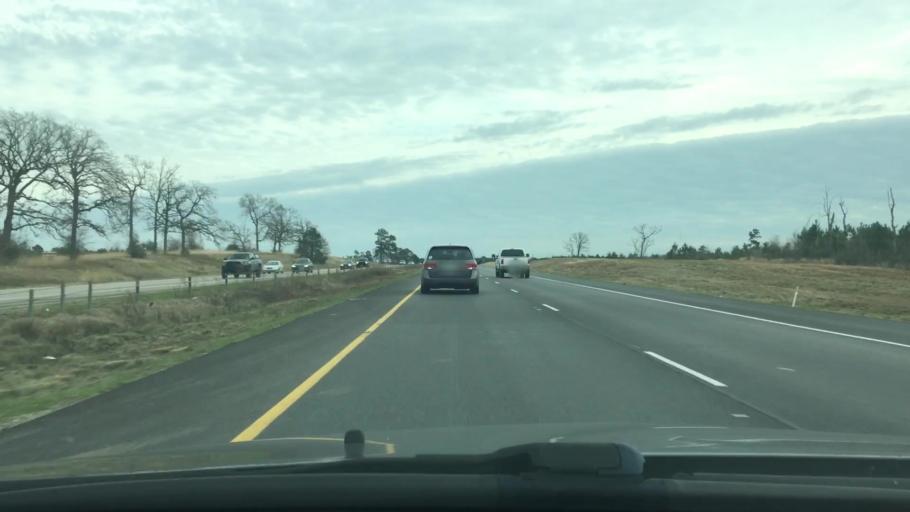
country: US
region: Texas
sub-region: Madison County
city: Madisonville
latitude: 30.8466
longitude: -95.7321
